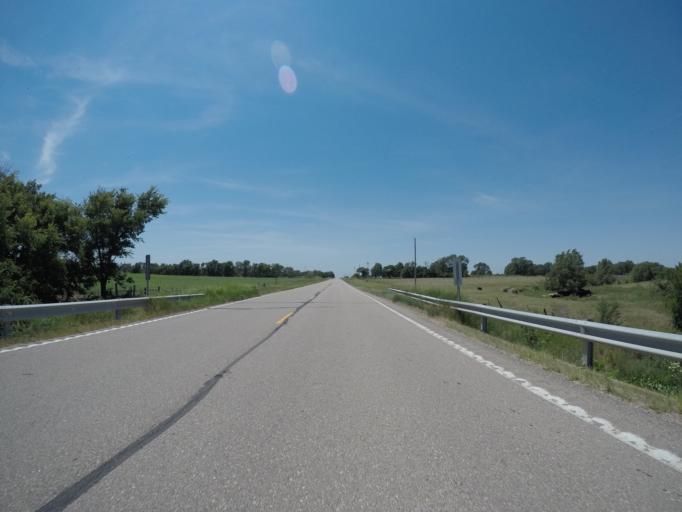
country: US
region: Kansas
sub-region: Ottawa County
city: Minneapolis
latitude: 39.0306
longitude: -97.5355
